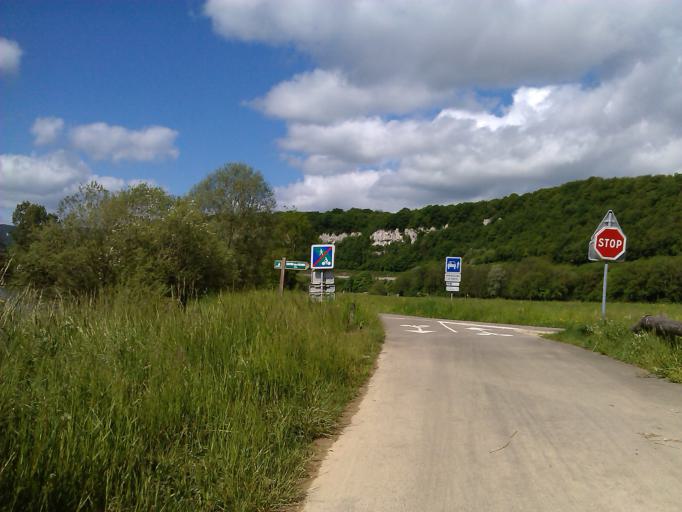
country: FR
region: Franche-Comte
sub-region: Departement du Doubs
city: Roulans
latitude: 47.3213
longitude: 6.2748
